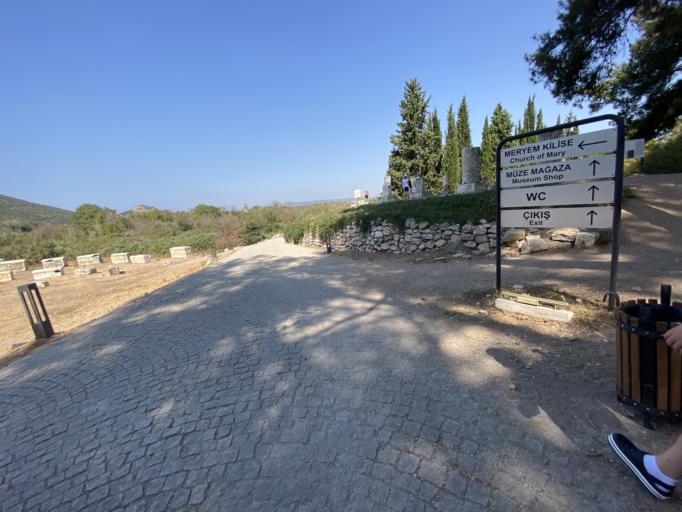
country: TR
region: Izmir
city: Selcuk
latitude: 37.9422
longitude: 27.3411
